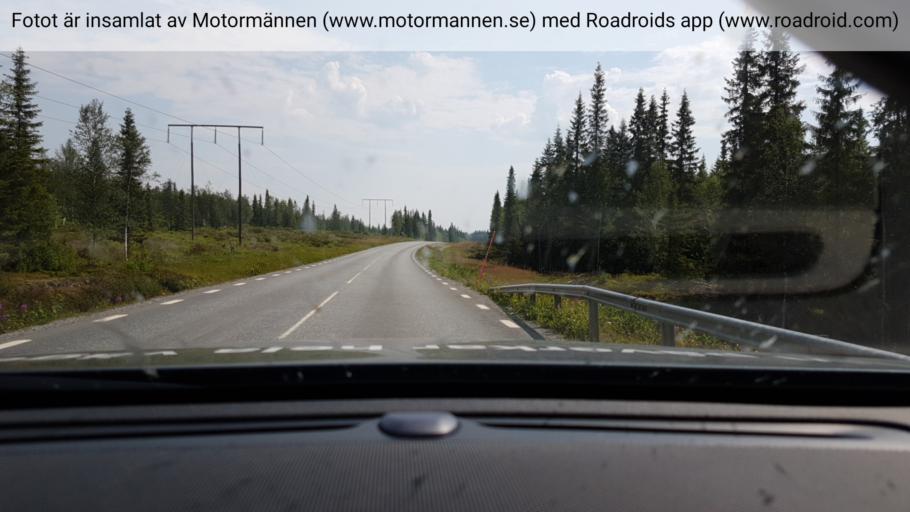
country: SE
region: Vaesterbotten
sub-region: Vilhelmina Kommun
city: Sjoberg
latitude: 65.4840
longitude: 15.8252
